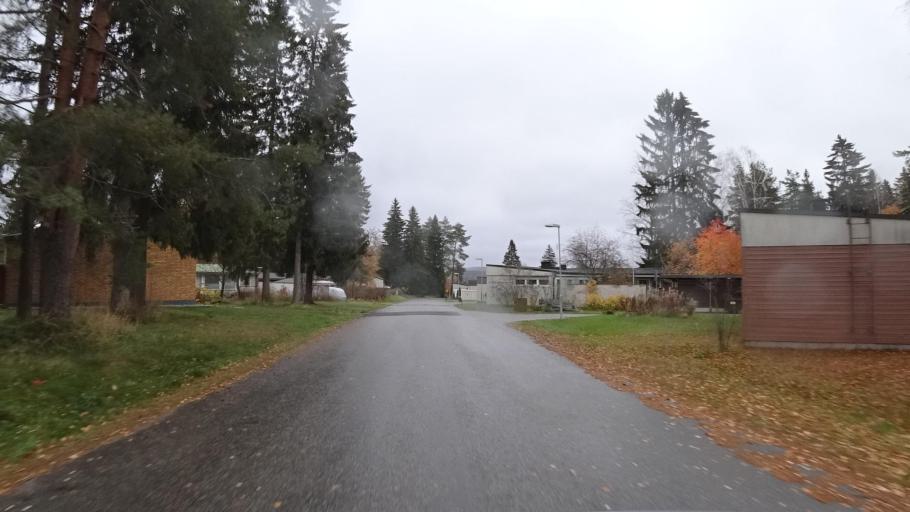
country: FI
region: Northern Savo
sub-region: Kuopio
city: Kuopio
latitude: 62.9281
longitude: 27.6902
